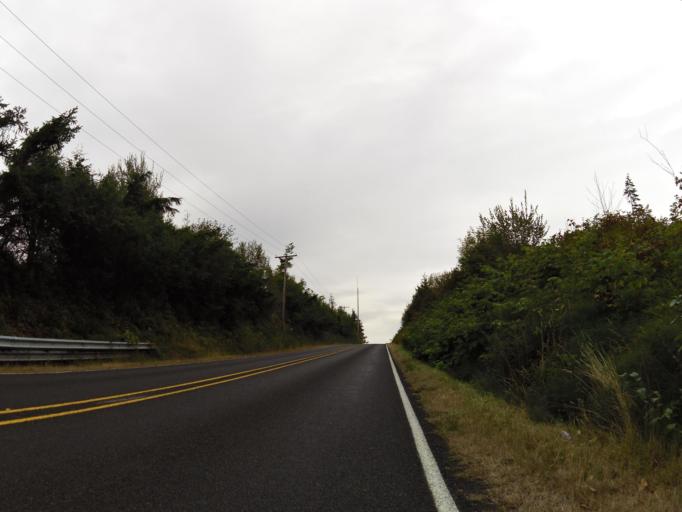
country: US
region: Washington
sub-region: Jefferson County
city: Port Ludlow
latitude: 47.9115
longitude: -122.6695
